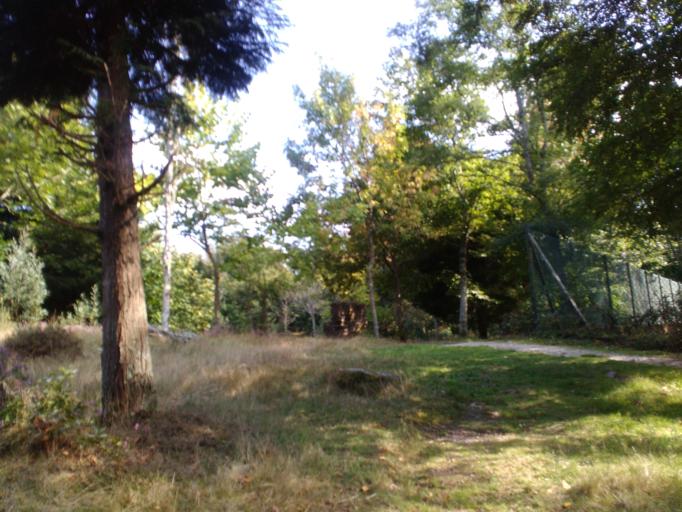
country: ES
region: Galicia
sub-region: Provincia de Pontevedra
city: Marin
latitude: 42.3597
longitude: -8.6762
